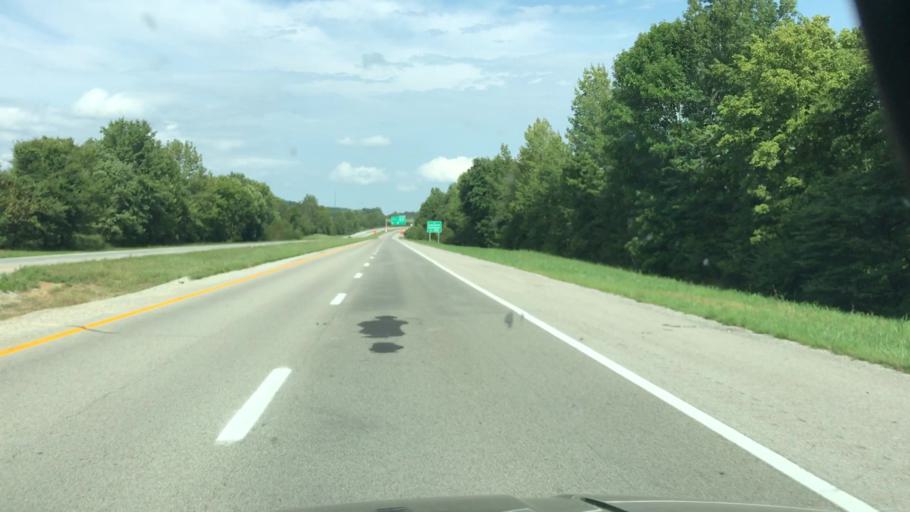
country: US
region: Kentucky
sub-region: Hopkins County
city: Nortonville
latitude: 37.2111
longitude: -87.4783
